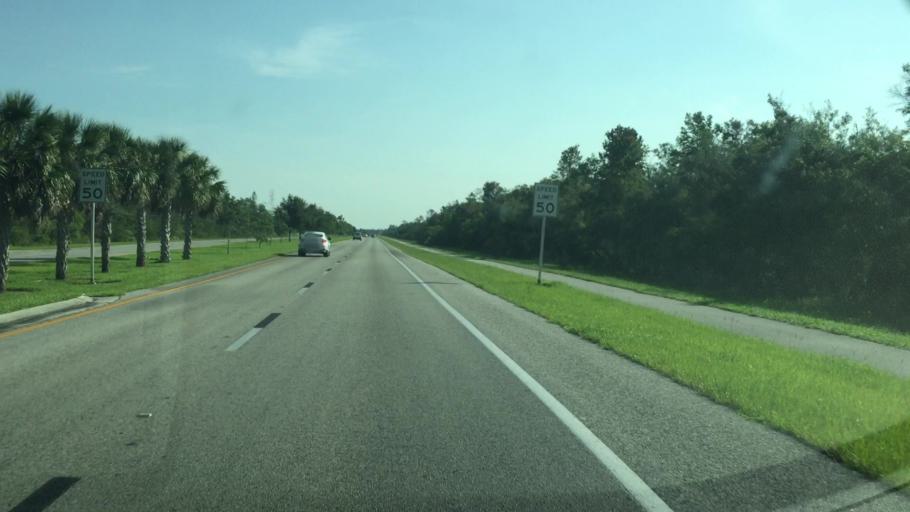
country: US
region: Florida
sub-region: Lee County
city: Villas
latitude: 26.5584
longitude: -81.8327
